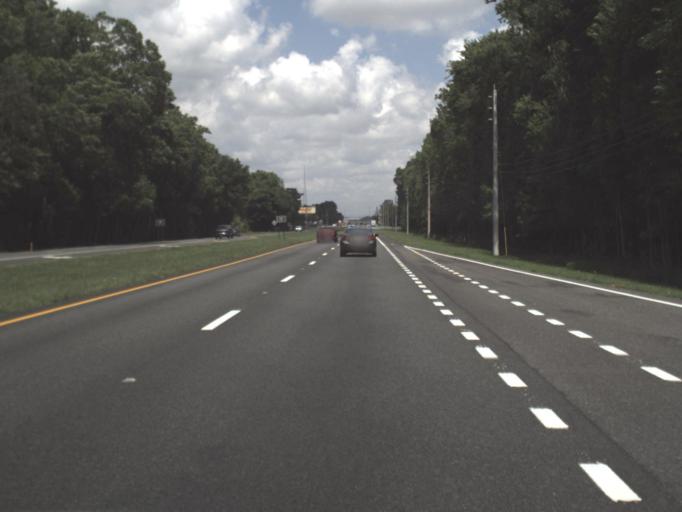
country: US
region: Florida
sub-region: Saint Johns County
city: Fruit Cove
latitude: 30.1527
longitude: -81.5266
